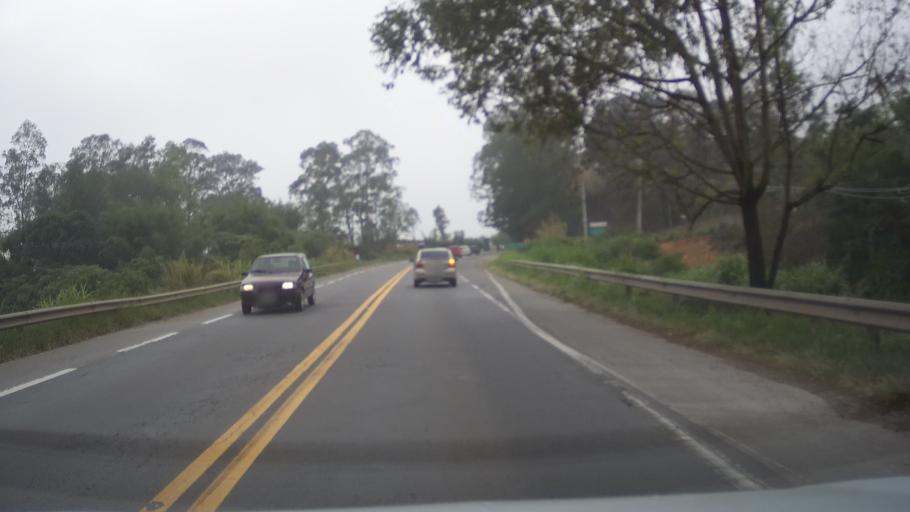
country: BR
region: Sao Paulo
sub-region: Itatiba
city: Itatiba
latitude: -22.9966
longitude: -46.8055
